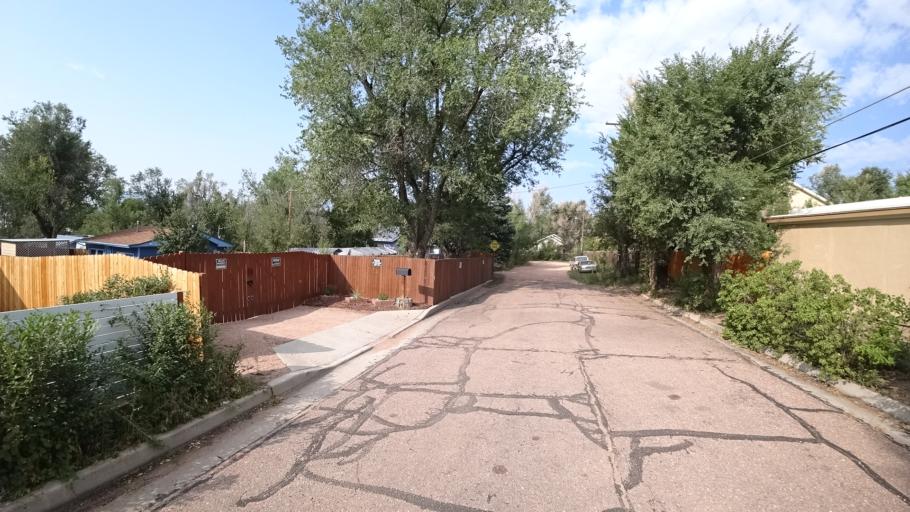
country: US
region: Colorado
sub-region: El Paso County
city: Colorado Springs
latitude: 38.8480
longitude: -104.7829
